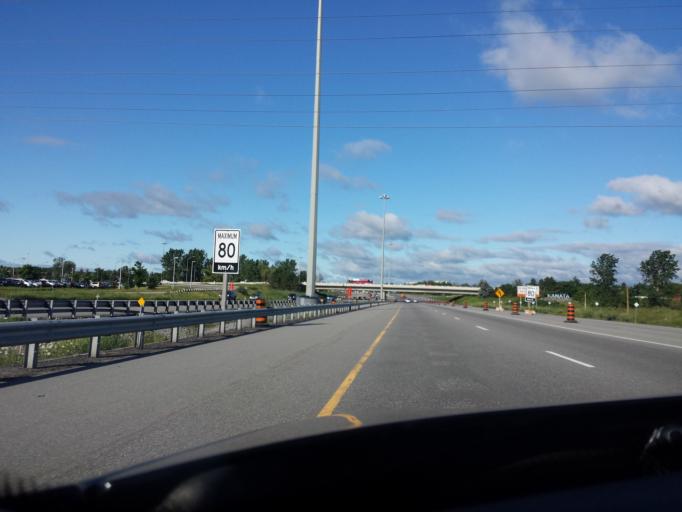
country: CA
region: Ontario
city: Bells Corners
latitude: 45.3218
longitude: -75.8825
